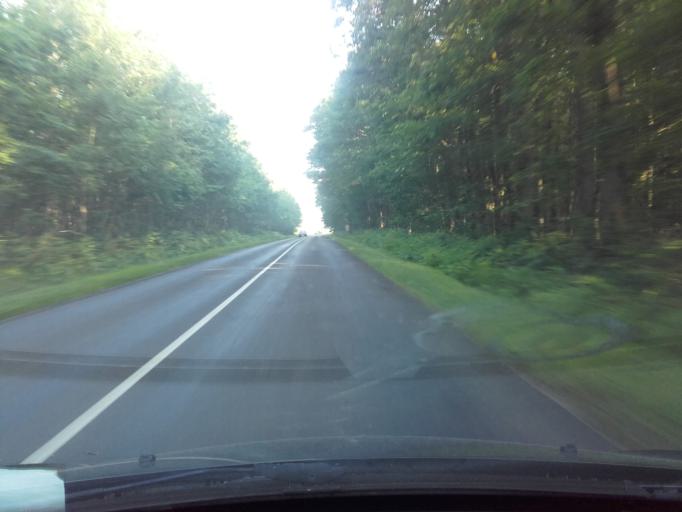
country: FR
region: Centre
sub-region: Departement d'Indre-et-Loire
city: Mazieres-de-Touraine
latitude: 47.3758
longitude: 0.4286
